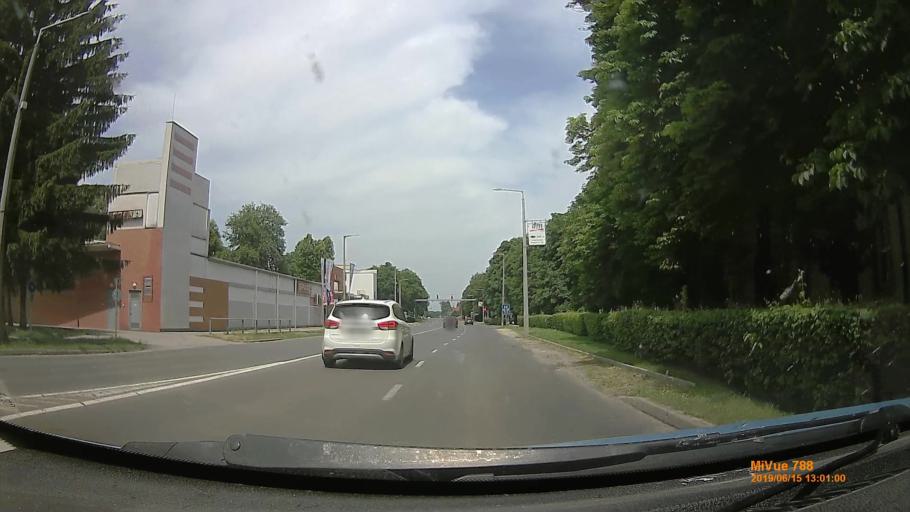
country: HU
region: Tolna
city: Dombovar
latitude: 46.3771
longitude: 18.1308
